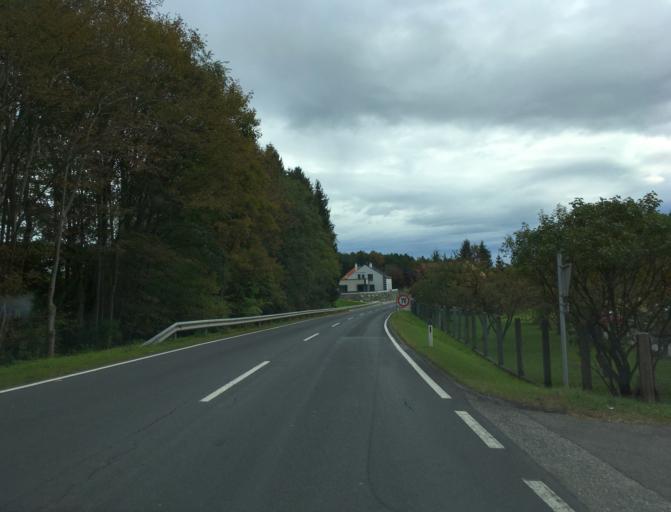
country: AT
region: Lower Austria
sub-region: Politischer Bezirk Neunkirchen
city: Thomasberg
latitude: 47.5378
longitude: 16.1639
